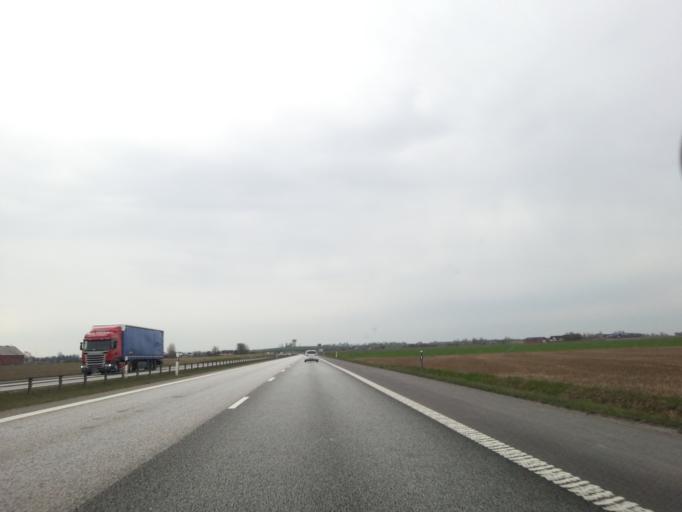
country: SE
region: Skane
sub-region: Angelholms Kommun
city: AEngelholm
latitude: 56.2784
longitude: 12.8967
